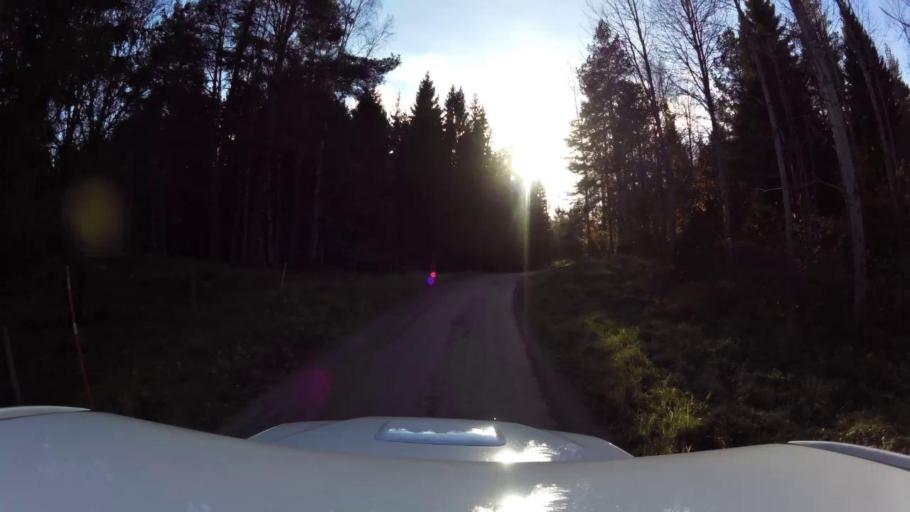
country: SE
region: OEstergoetland
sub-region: Linkopings Kommun
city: Vikingstad
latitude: 58.2144
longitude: 15.4396
